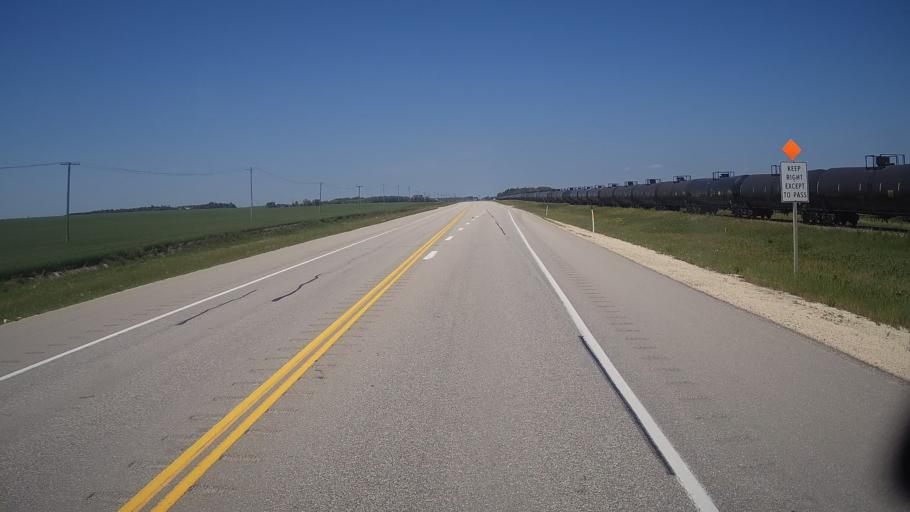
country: CA
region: Manitoba
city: Stonewall
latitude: 50.0984
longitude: -97.4950
